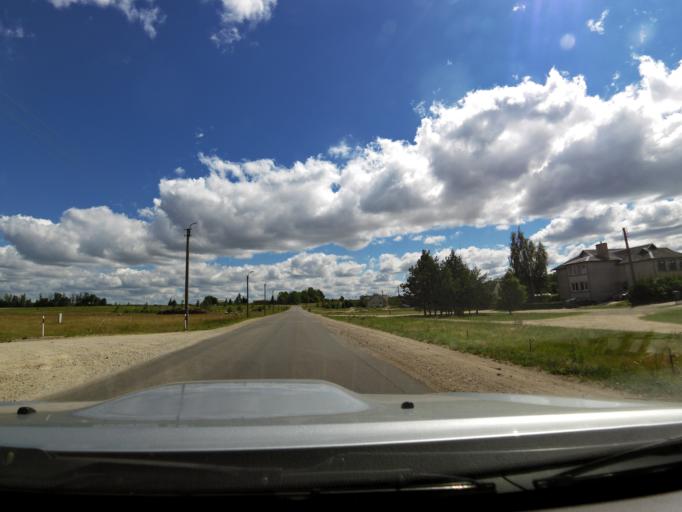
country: LT
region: Panevezys
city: Rokiskis
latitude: 55.9688
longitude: 25.5925
